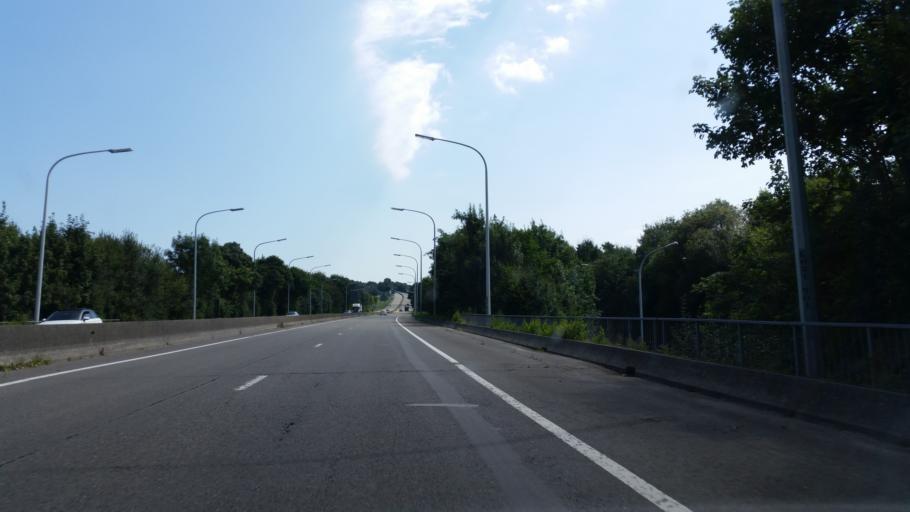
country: BE
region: Wallonia
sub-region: Province de Namur
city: Hamois
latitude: 50.3184
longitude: 5.1291
